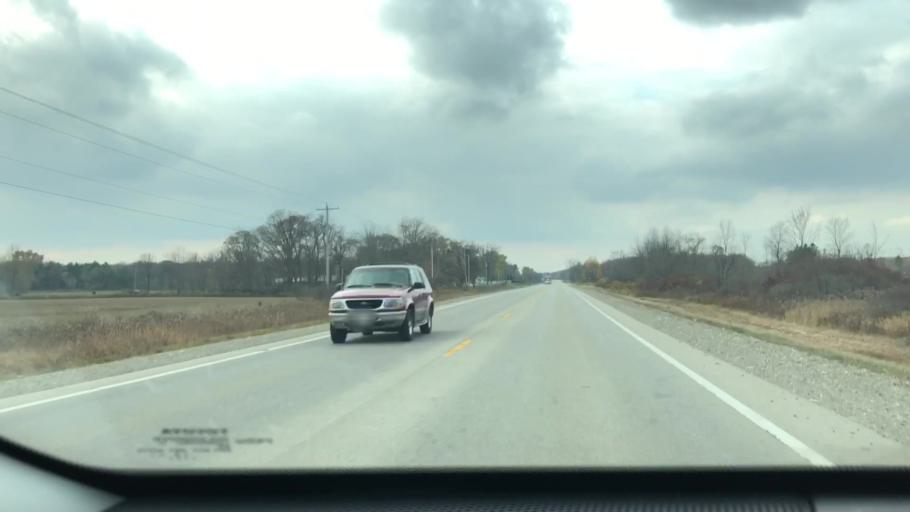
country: US
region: Wisconsin
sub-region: Brown County
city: Oneida
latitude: 44.5022
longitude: -88.2256
